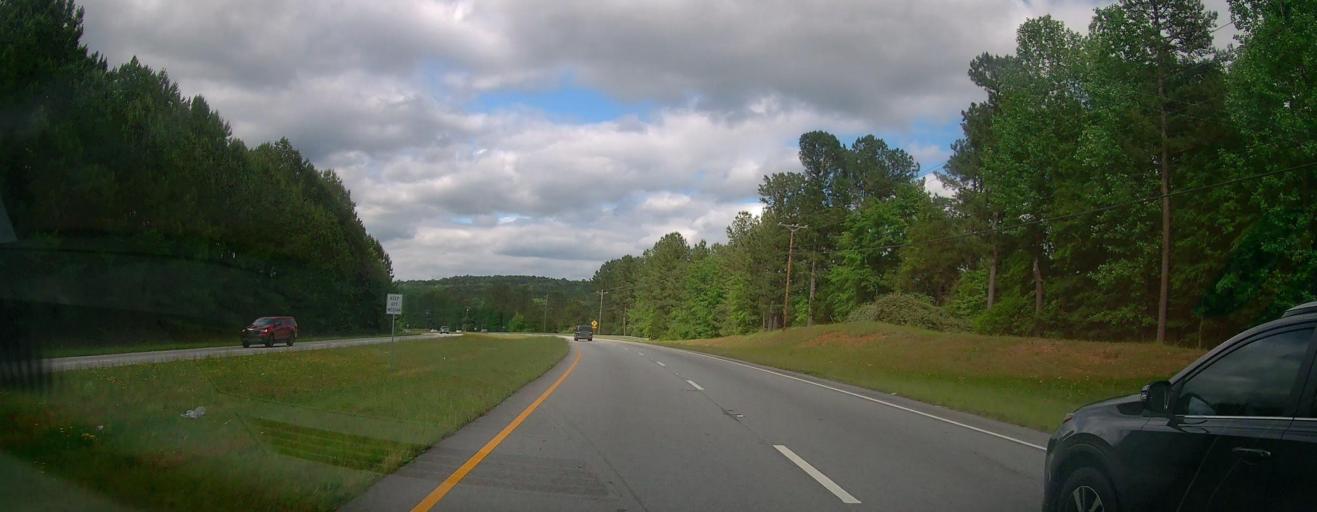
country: US
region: Georgia
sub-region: Rockdale County
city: Conyers
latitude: 33.6818
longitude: -83.9640
